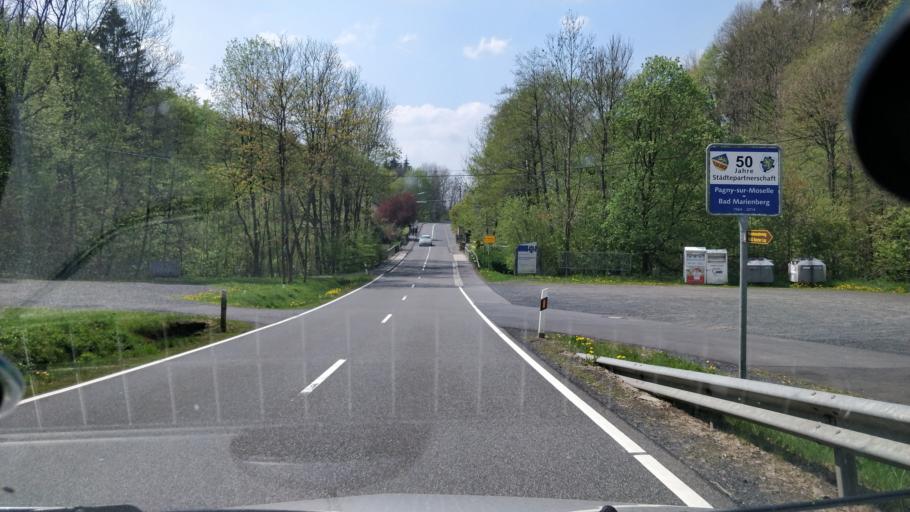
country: DE
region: Rheinland-Pfalz
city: Bad Marienberg
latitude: 50.6489
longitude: 7.9598
